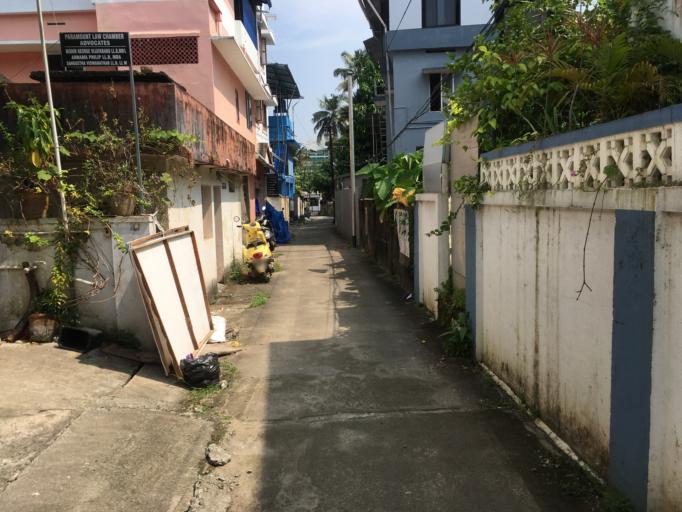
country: IN
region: Kerala
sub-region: Ernakulam
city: Cochin
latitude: 9.9867
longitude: 76.2773
